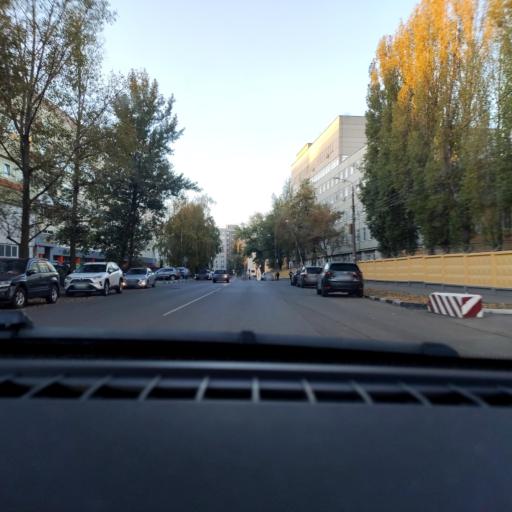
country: RU
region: Voronezj
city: Voronezh
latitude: 51.6763
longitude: 39.2510
